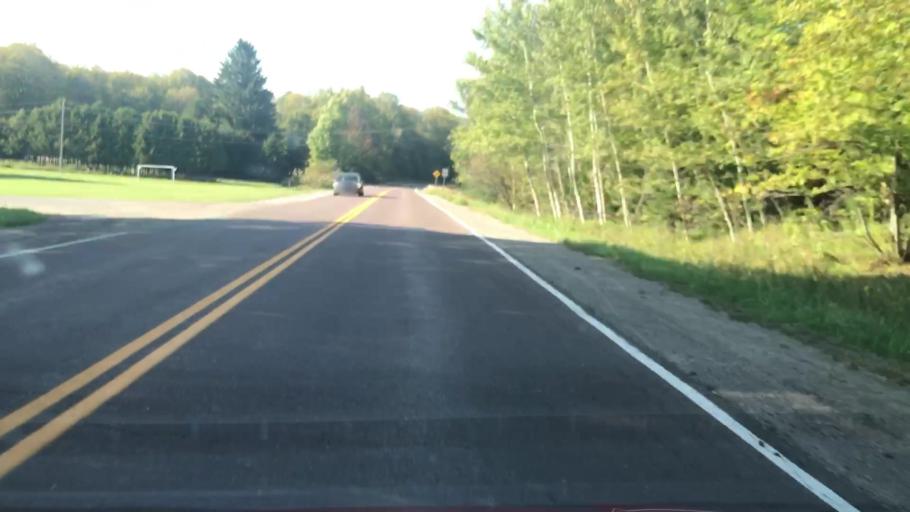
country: US
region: Michigan
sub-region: Chippewa County
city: Sault Ste. Marie
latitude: 46.2792
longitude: -84.0307
